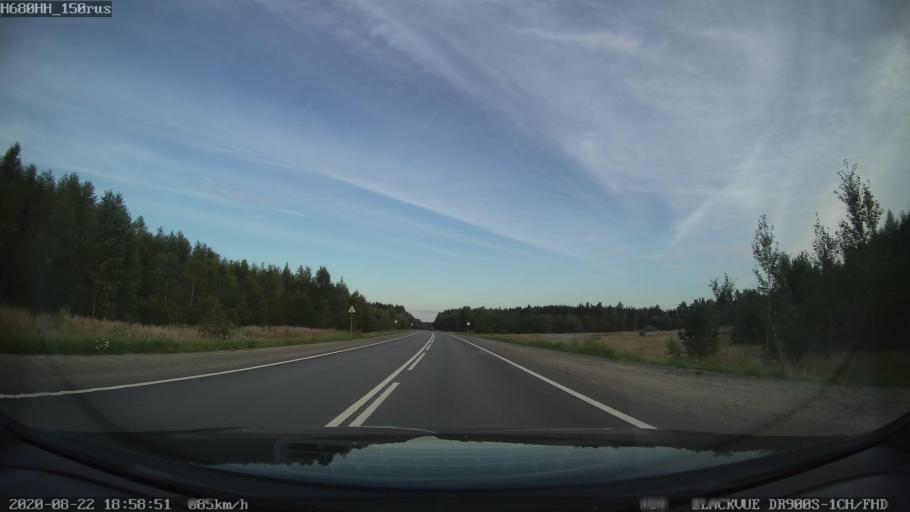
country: RU
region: Tverskaya
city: Rameshki
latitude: 57.1496
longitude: 36.0821
